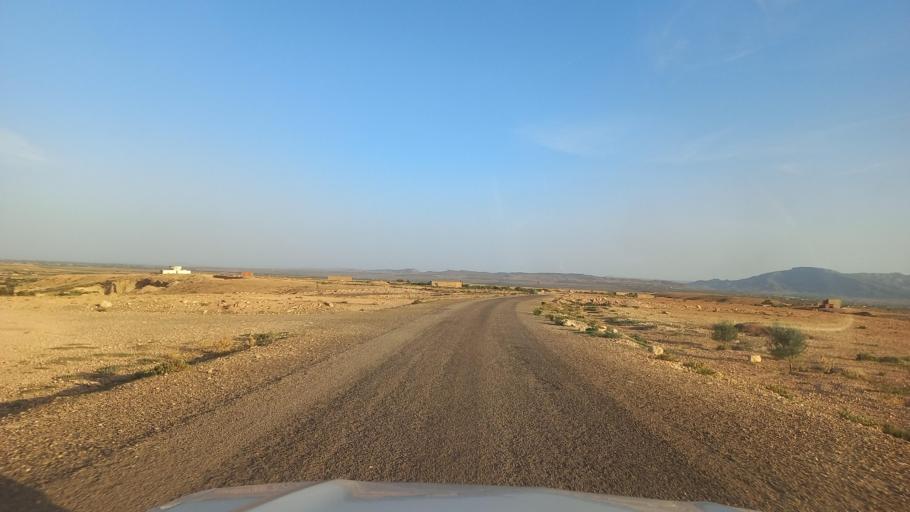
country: TN
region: Al Qasrayn
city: Kasserine
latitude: 35.2748
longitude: 8.9130
